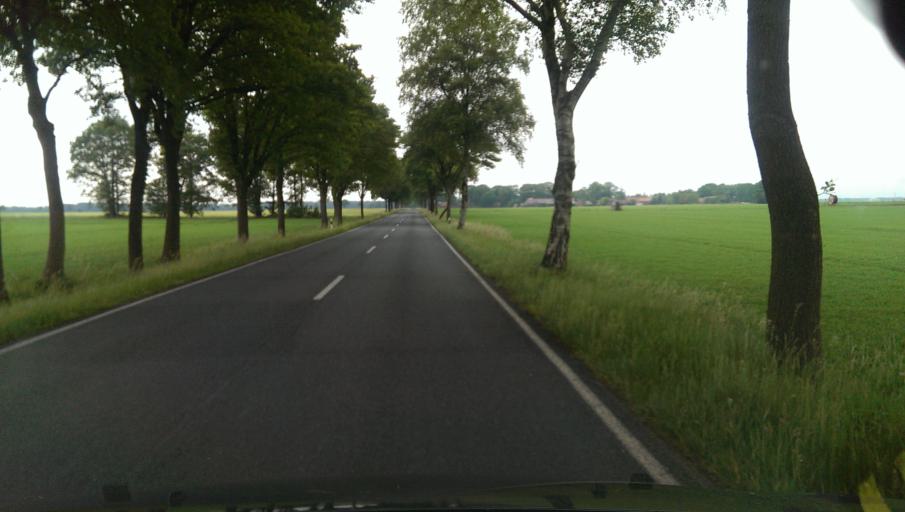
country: DE
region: Lower Saxony
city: Sprakensehl
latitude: 52.7488
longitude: 10.5291
